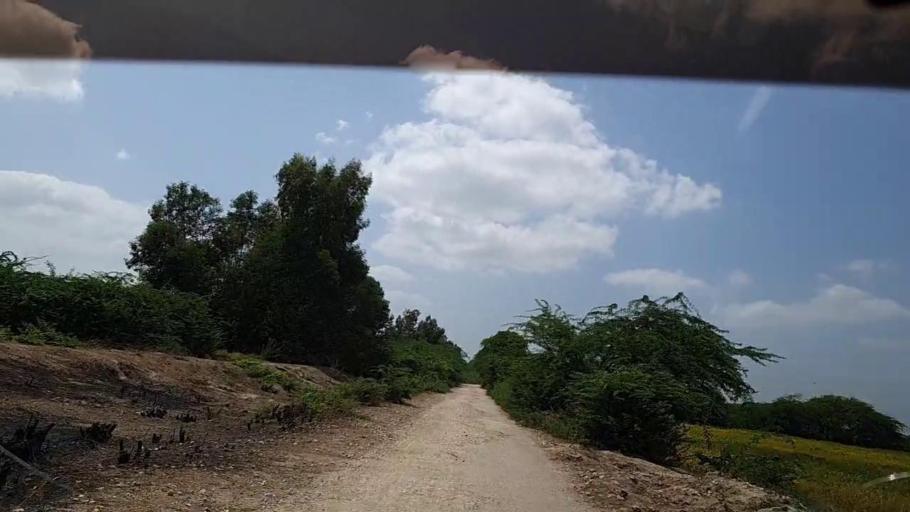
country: PK
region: Sindh
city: Badin
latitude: 24.5782
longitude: 68.7801
